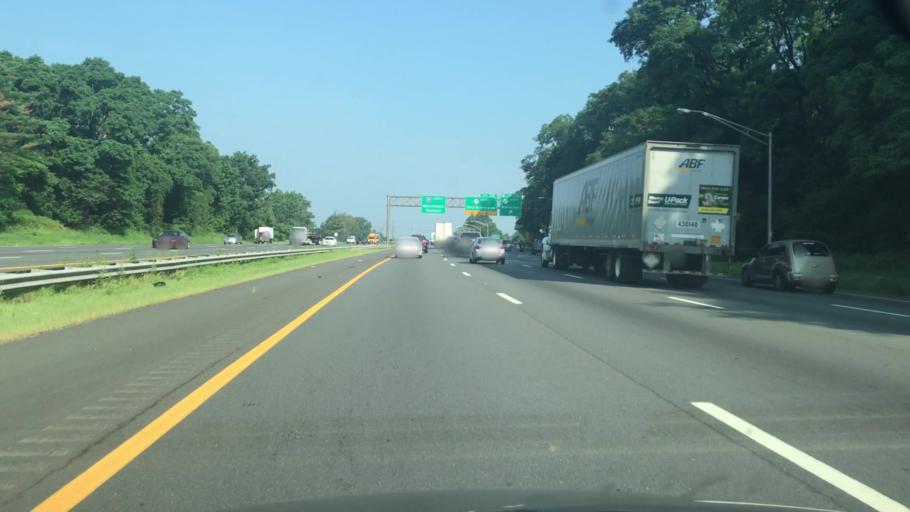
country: US
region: New Jersey
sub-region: Middlesex County
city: Metuchen
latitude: 40.5311
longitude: -74.3726
